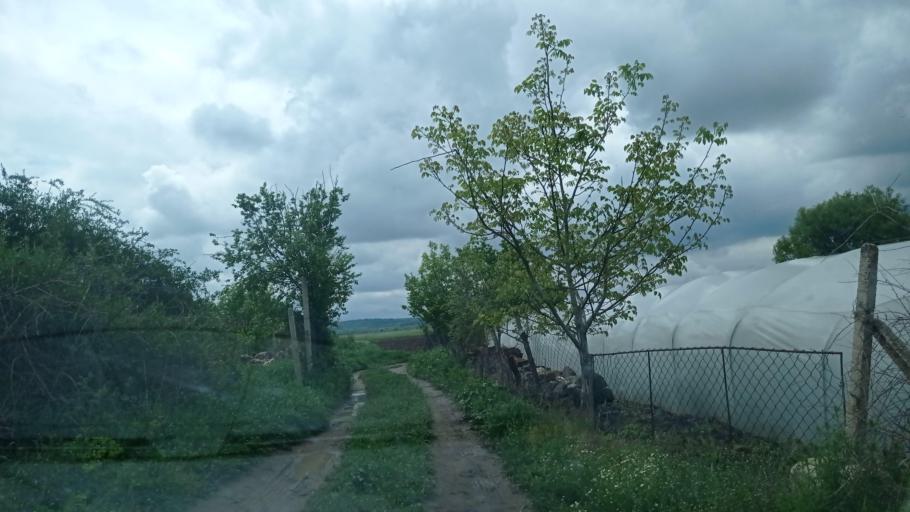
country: MK
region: Lozovo
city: Lozovo
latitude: 41.7645
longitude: 21.8909
